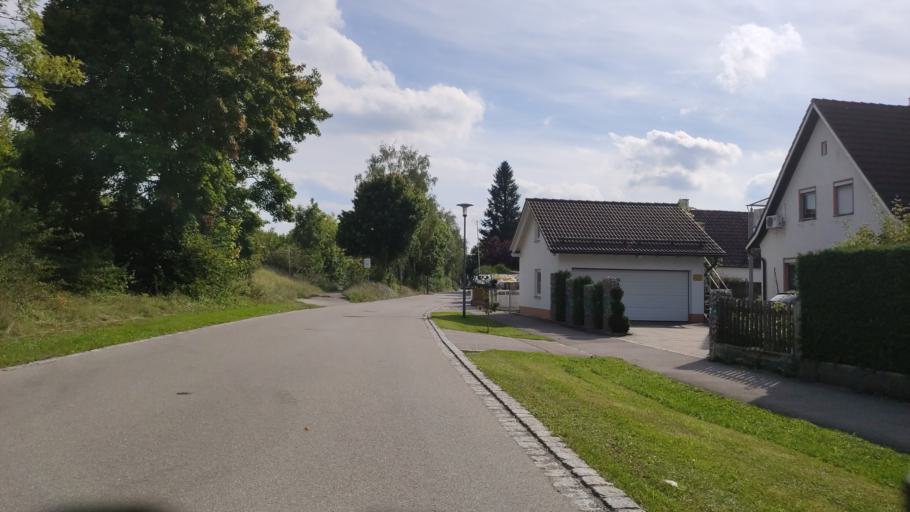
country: DE
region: Bavaria
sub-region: Swabia
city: Klosterlechfeld
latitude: 48.1547
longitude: 10.8320
